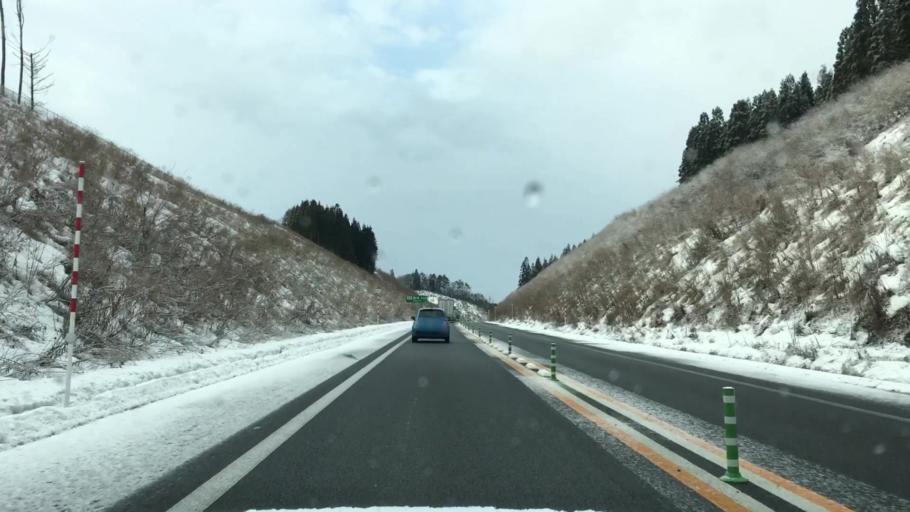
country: JP
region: Akita
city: Takanosu
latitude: 40.2140
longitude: 140.4201
